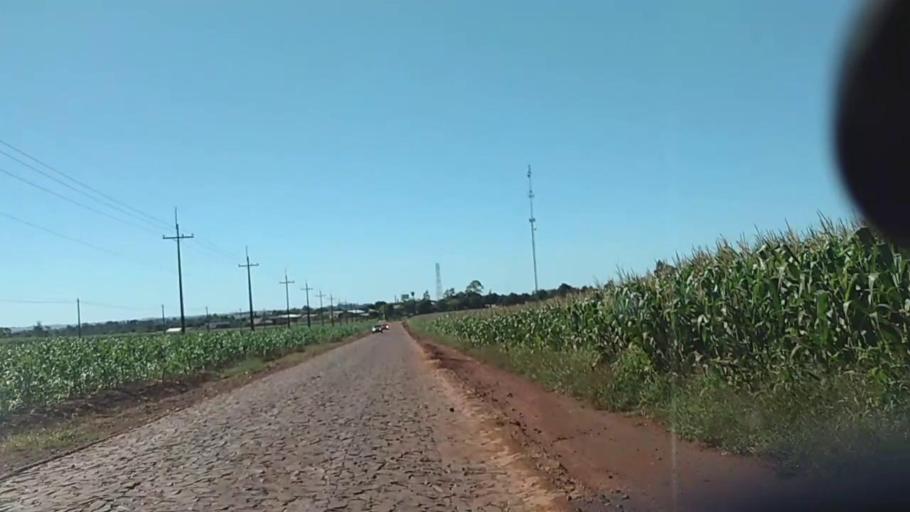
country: PY
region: Alto Parana
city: Naranjal
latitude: -25.9730
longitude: -55.2042
